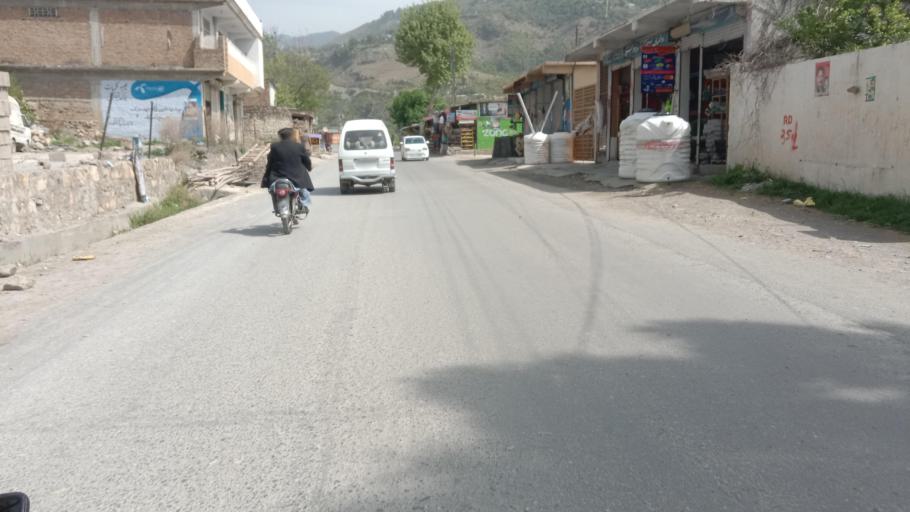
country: PK
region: Khyber Pakhtunkhwa
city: Abbottabad
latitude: 34.1403
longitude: 73.2842
